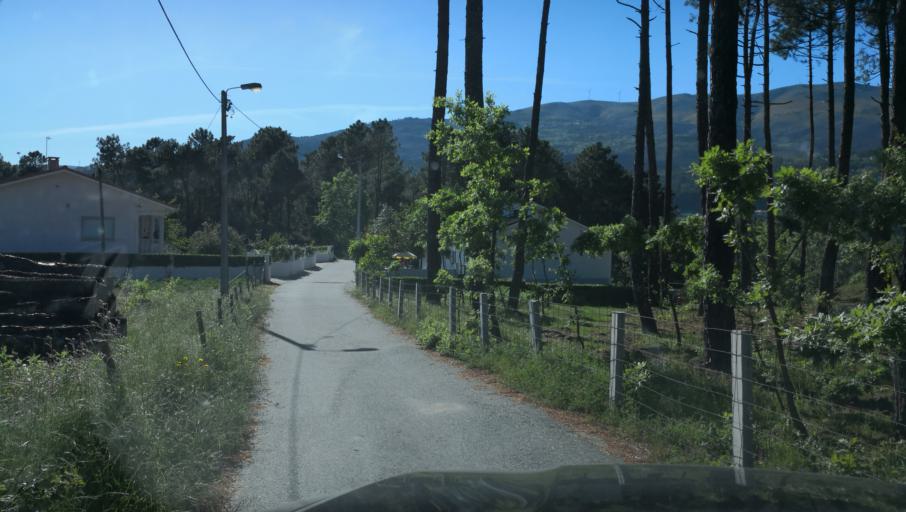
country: PT
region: Vila Real
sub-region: Vila Real
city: Vila Real
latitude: 41.3334
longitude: -7.7314
